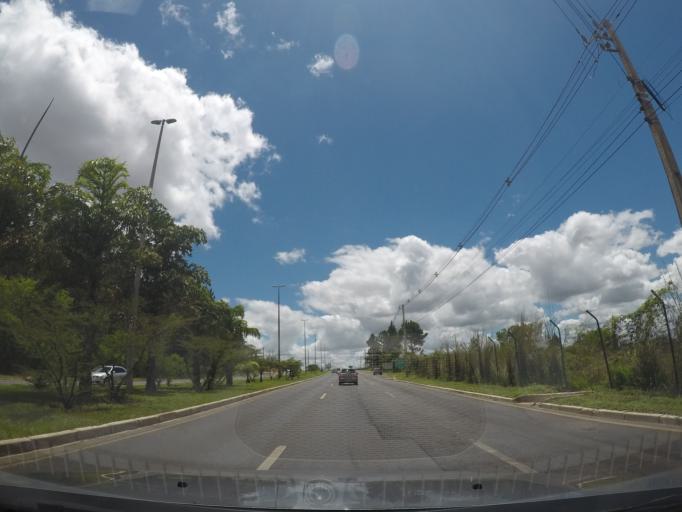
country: BR
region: Federal District
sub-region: Brasilia
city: Brasilia
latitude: -15.8387
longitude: -47.9594
